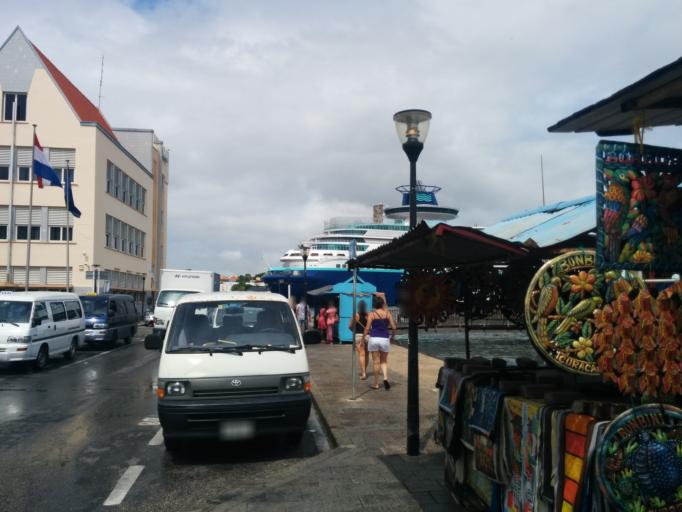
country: CW
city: Willemstad
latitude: 12.1065
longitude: -68.9329
